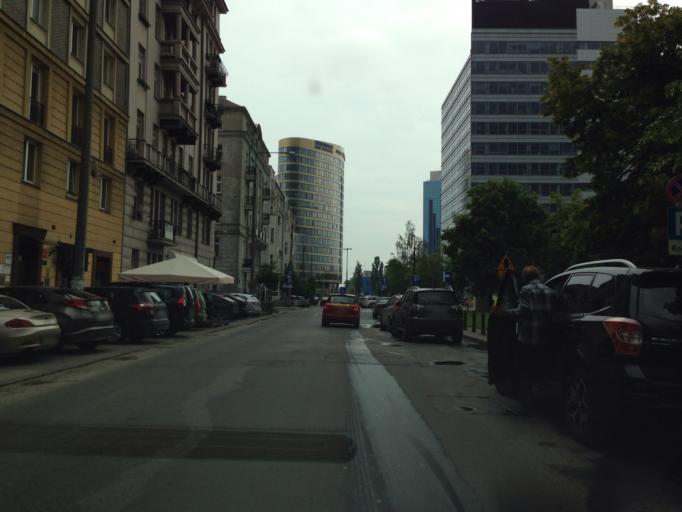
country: PL
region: Masovian Voivodeship
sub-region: Warszawa
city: Srodmiescie
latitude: 52.2192
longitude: 21.0133
